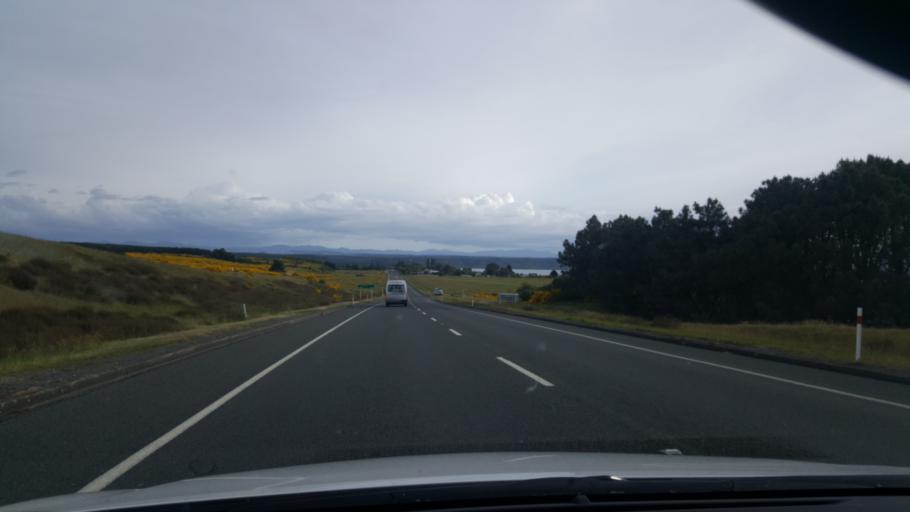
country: NZ
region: Waikato
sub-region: Taupo District
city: Taupo
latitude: -38.7438
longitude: 176.0732
